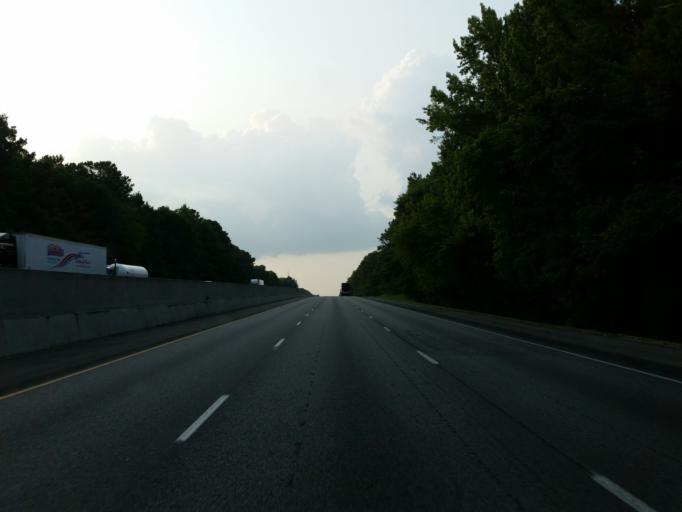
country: US
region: Georgia
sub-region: Bibb County
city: West Point
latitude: 32.9161
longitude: -83.7970
